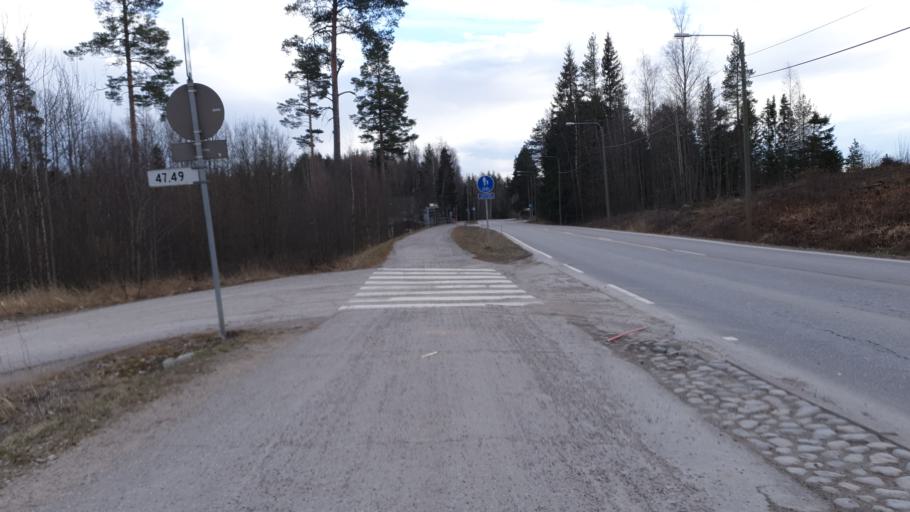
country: FI
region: Uusimaa
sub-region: Helsinki
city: Tuusula
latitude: 60.3429
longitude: 24.9199
